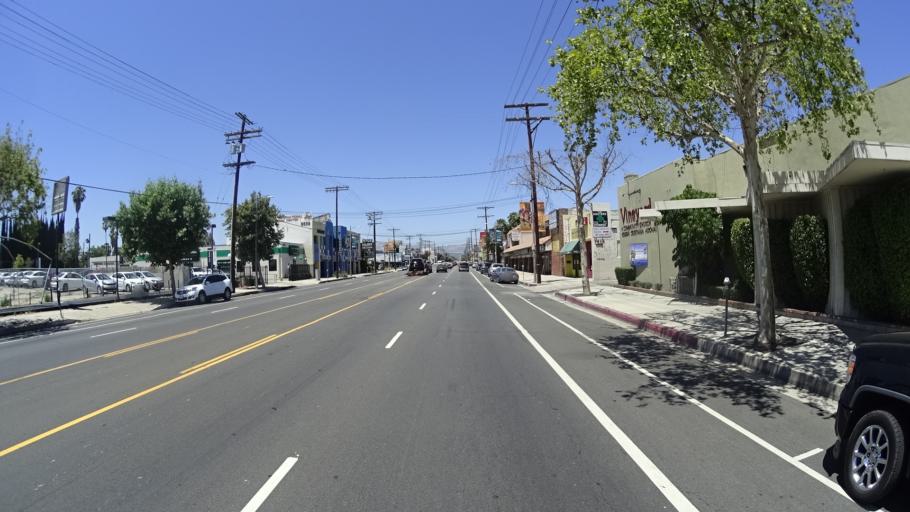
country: US
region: California
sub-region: Los Angeles County
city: Northridge
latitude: 34.1913
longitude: -118.5359
